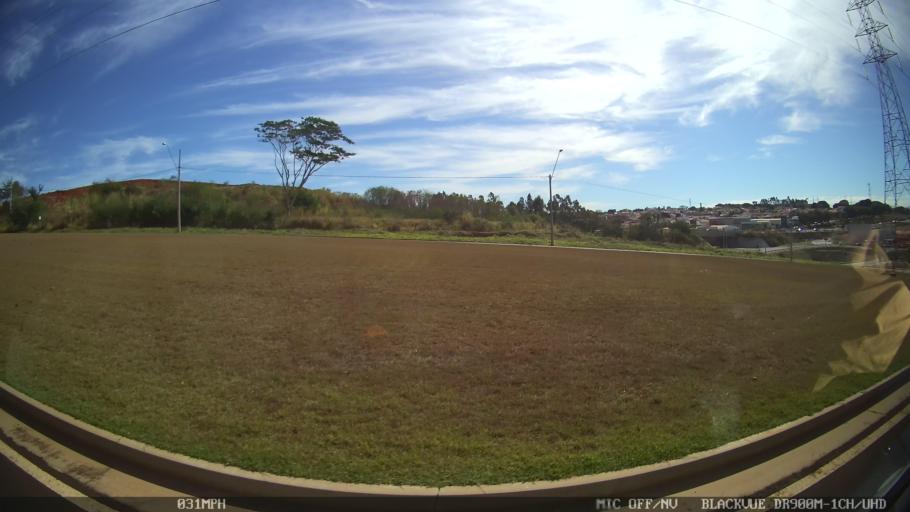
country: BR
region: Sao Paulo
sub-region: Sao Jose Do Rio Preto
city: Sao Jose do Rio Preto
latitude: -20.8492
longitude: -49.3740
